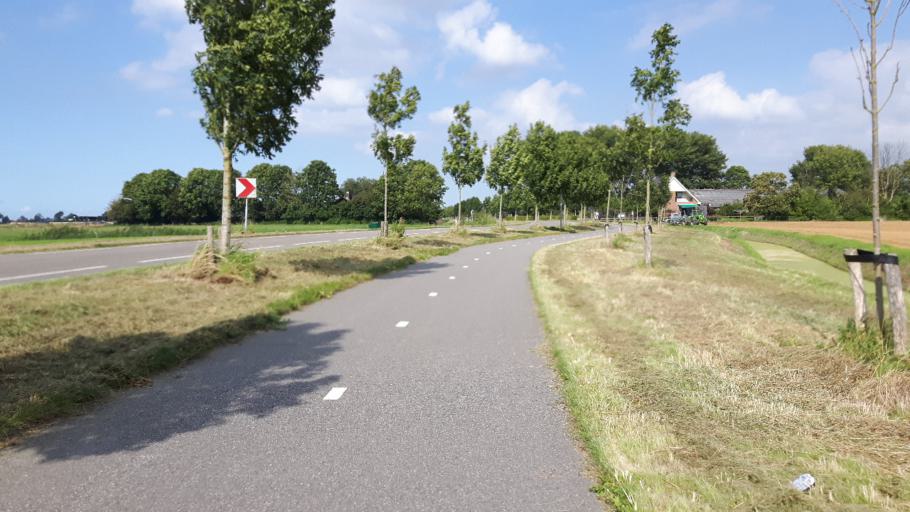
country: NL
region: North Holland
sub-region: Gemeente Medemblik
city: Opperdoes
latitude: 52.7134
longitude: 5.0916
